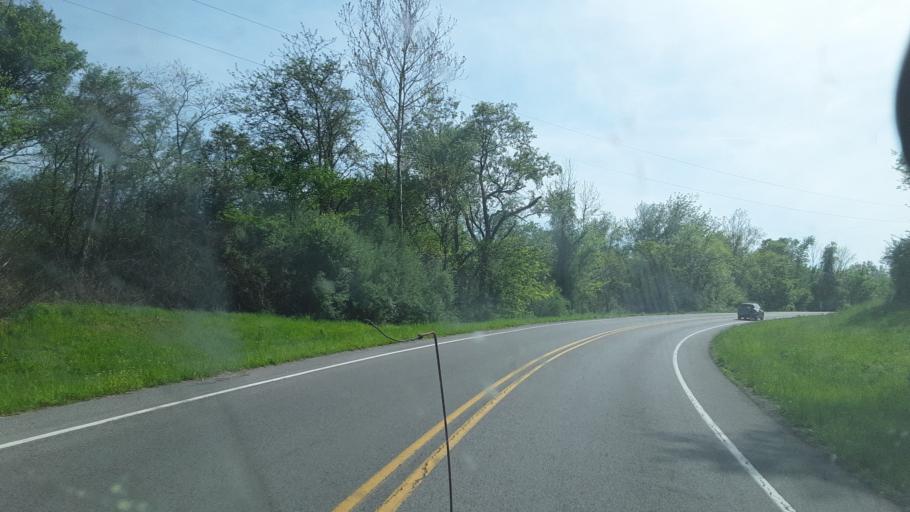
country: US
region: Illinois
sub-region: Jackson County
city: Carbondale
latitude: 37.6888
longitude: -89.2477
